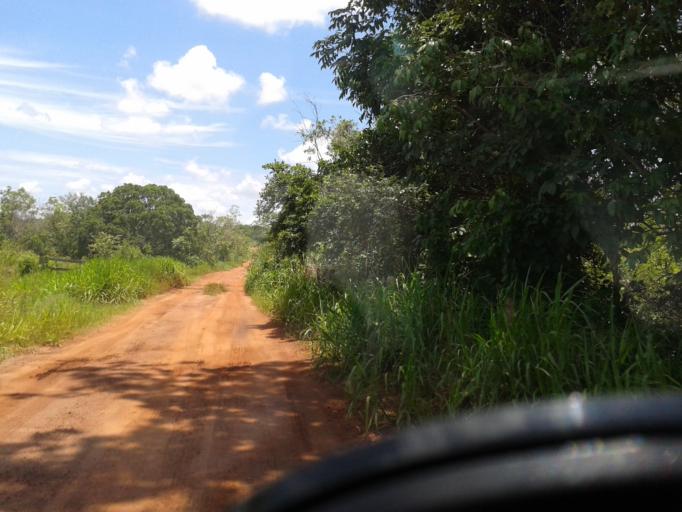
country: BR
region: Minas Gerais
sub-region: Santa Vitoria
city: Santa Vitoria
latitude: -18.9622
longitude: -49.8698
